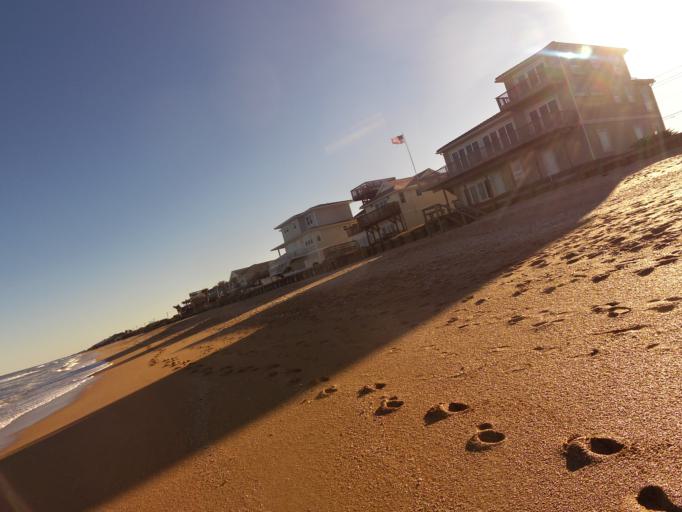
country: US
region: Florida
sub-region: Saint Johns County
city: Villano Beach
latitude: 29.9956
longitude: -81.3159
